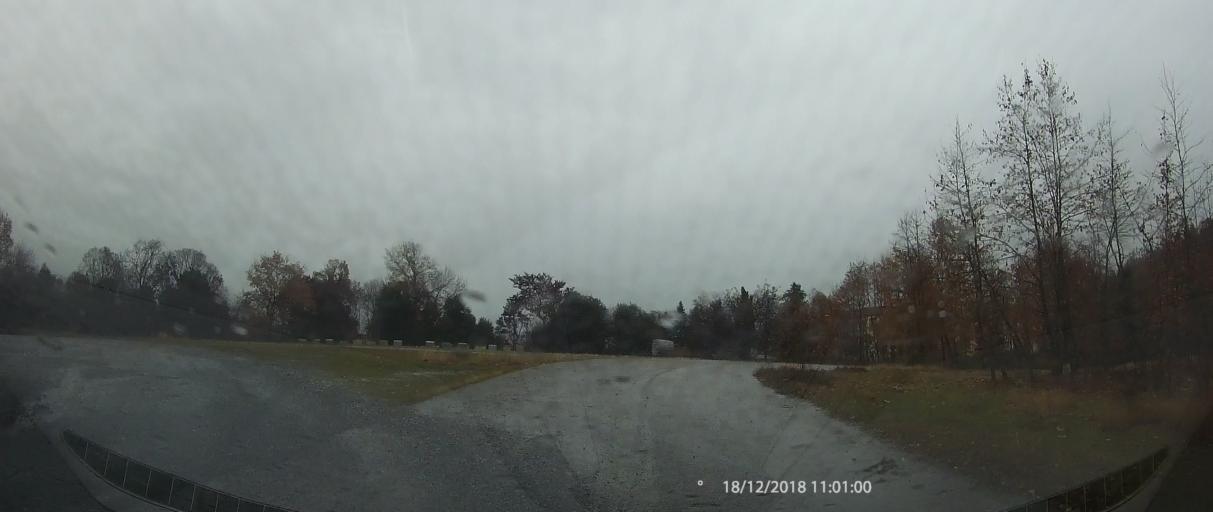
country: GR
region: Central Macedonia
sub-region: Nomos Pierias
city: Kato Milia
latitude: 40.1995
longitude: 22.3172
